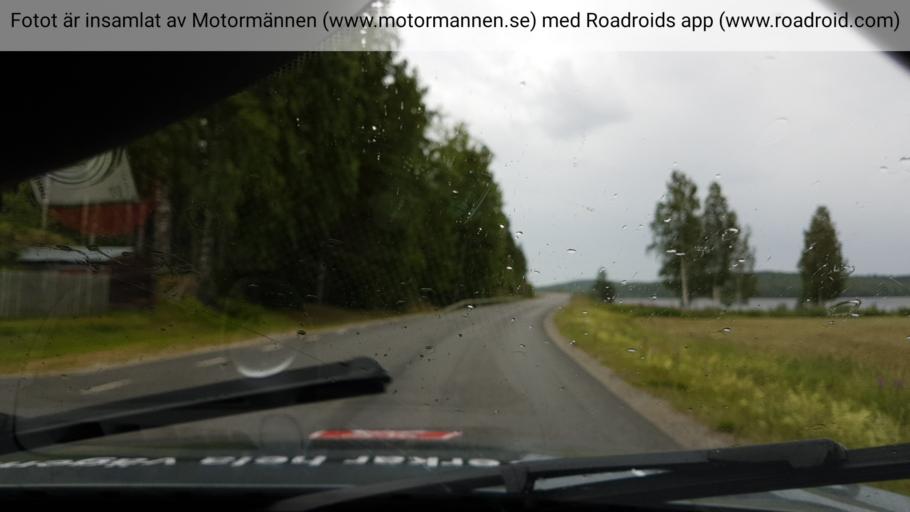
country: SE
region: Jaemtland
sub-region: Braecke Kommun
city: Braecke
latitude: 62.3994
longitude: 15.0263
